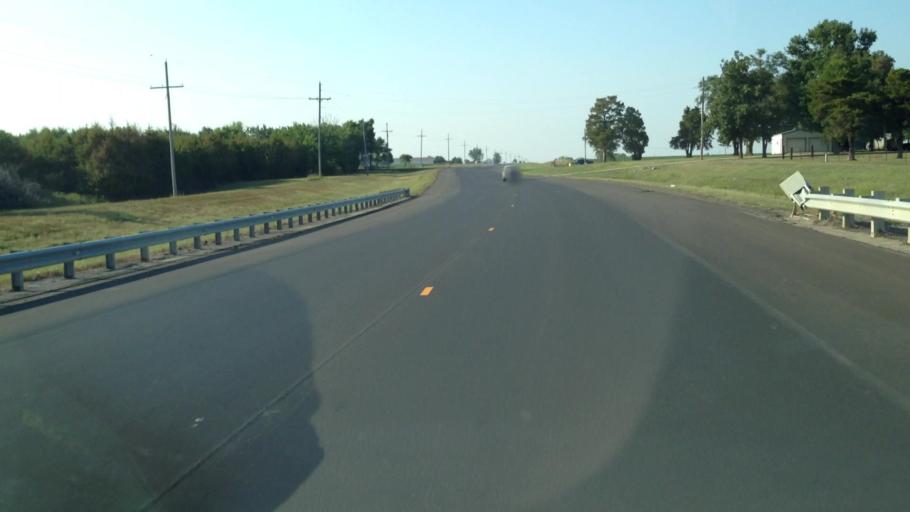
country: US
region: Kansas
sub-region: Franklin County
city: Ottawa
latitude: 38.4969
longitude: -95.2672
